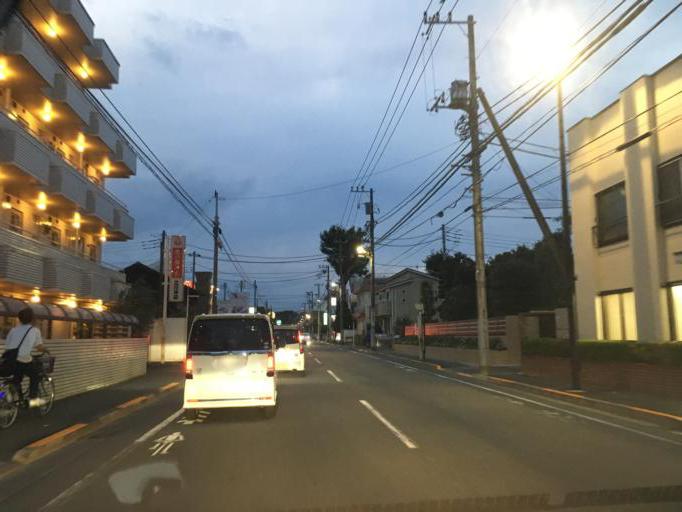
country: JP
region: Tokyo
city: Higashimurayama-shi
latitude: 35.7309
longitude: 139.4567
